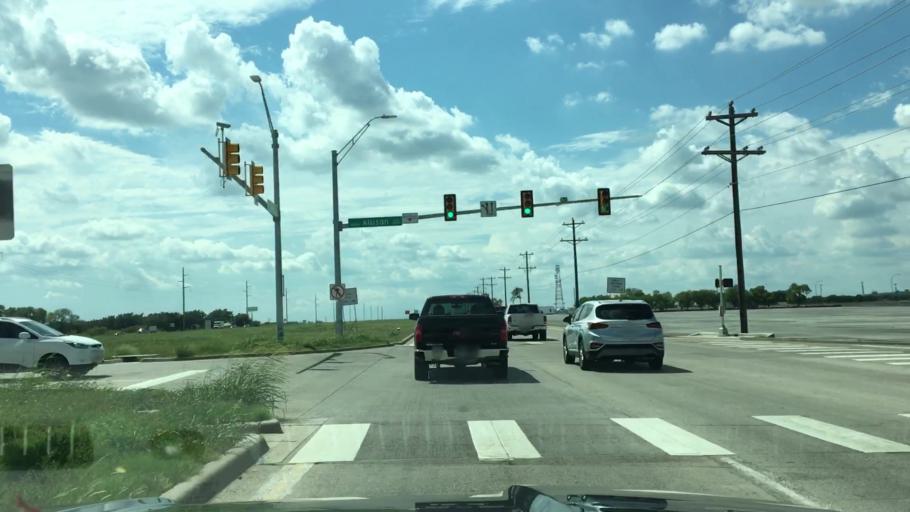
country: US
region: Texas
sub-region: Denton County
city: Justin
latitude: 33.0269
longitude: -97.2833
